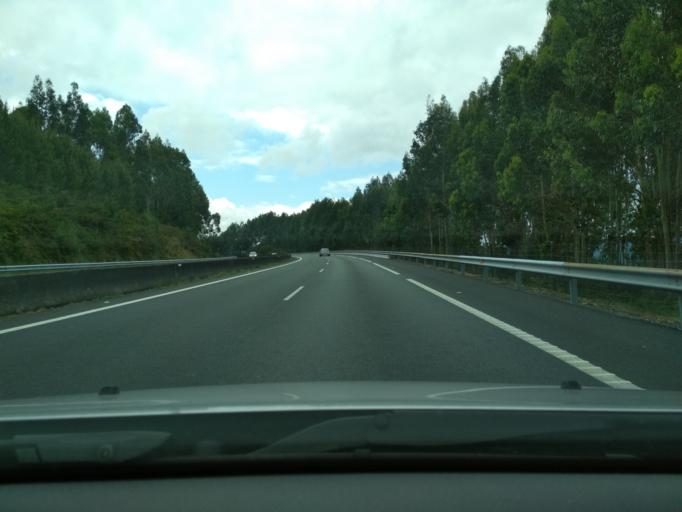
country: ES
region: Galicia
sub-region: Provincia da Coruna
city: Padron
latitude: 42.7854
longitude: -8.6438
